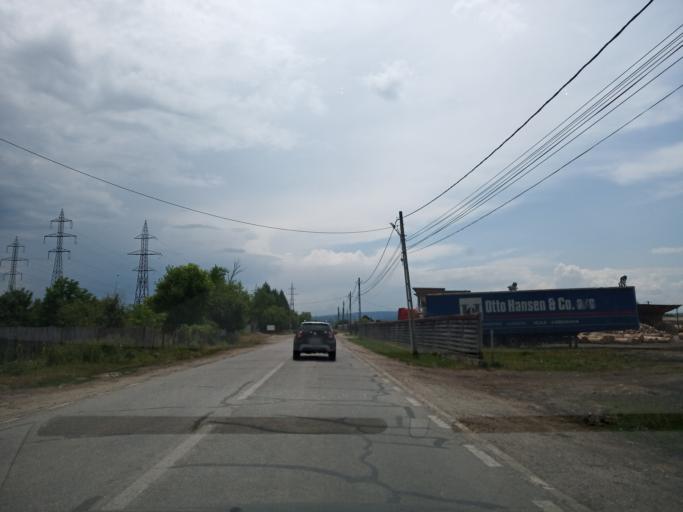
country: RO
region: Gorj
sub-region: Comuna Tismana
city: Tismana
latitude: 45.0377
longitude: 22.9505
